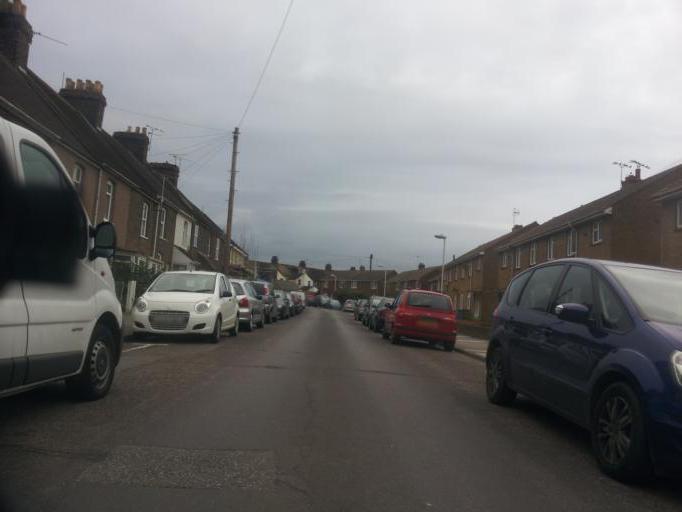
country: GB
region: England
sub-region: Kent
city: Sittingbourne
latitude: 51.3425
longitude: 0.7587
